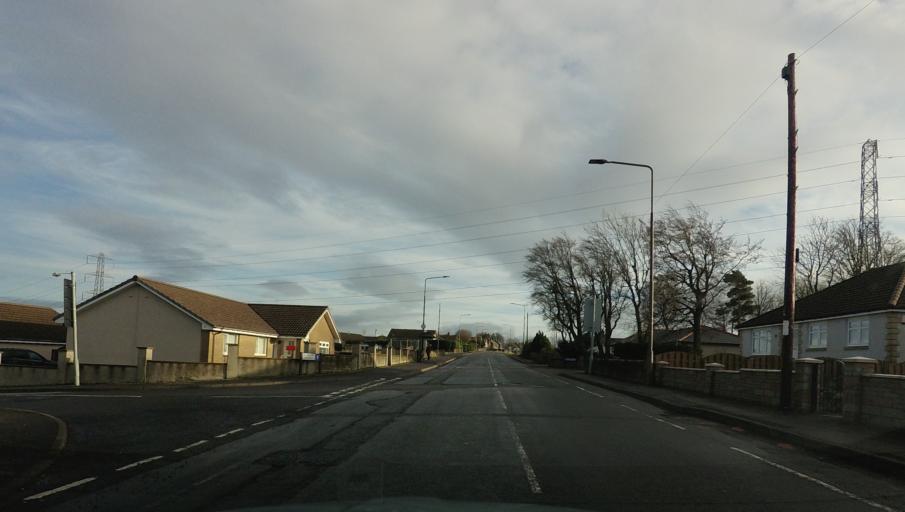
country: GB
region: Scotland
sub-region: West Lothian
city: Kirknewton
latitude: 55.8883
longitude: -3.4283
